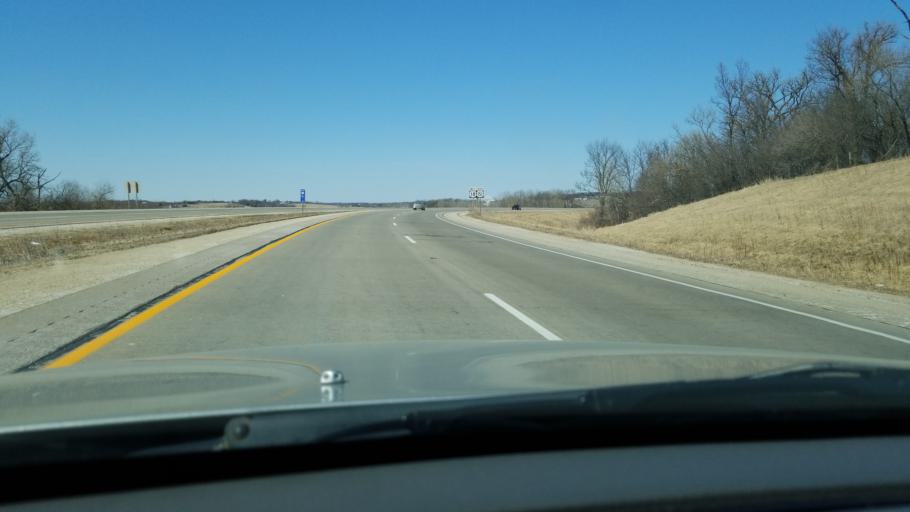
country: US
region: Wisconsin
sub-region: Dane County
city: Verona
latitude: 42.9765
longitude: -89.5543
